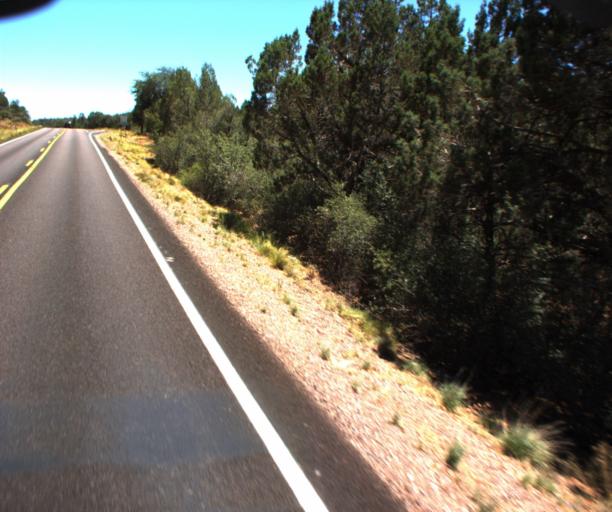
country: US
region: Arizona
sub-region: Gila County
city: Payson
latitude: 34.2901
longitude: -111.3450
